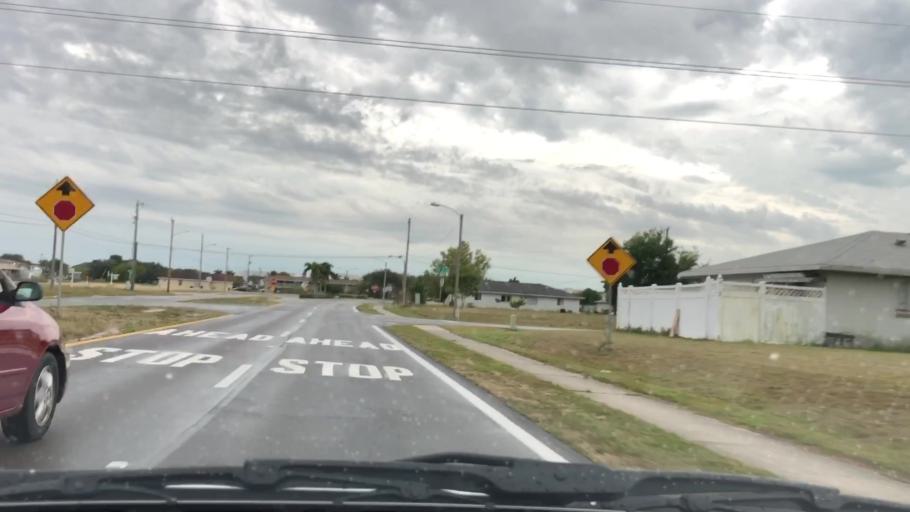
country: US
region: Florida
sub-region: Lee County
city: Lochmoor Waterway Estates
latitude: 26.6374
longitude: -81.9588
